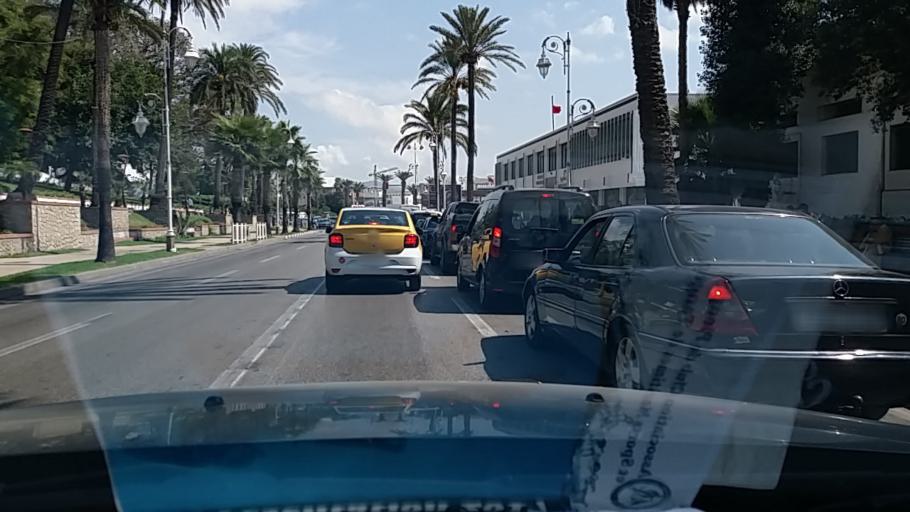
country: MA
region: Tanger-Tetouan
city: Tetouan
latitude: 35.5671
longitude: -5.3688
